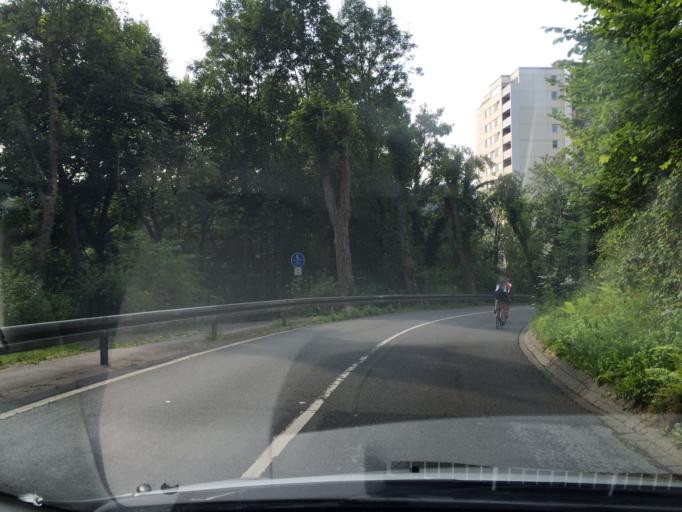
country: DE
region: North Rhine-Westphalia
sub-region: Regierungsbezirk Arnsberg
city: Nachrodt-Wiblingwerde
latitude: 51.3601
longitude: 7.6036
